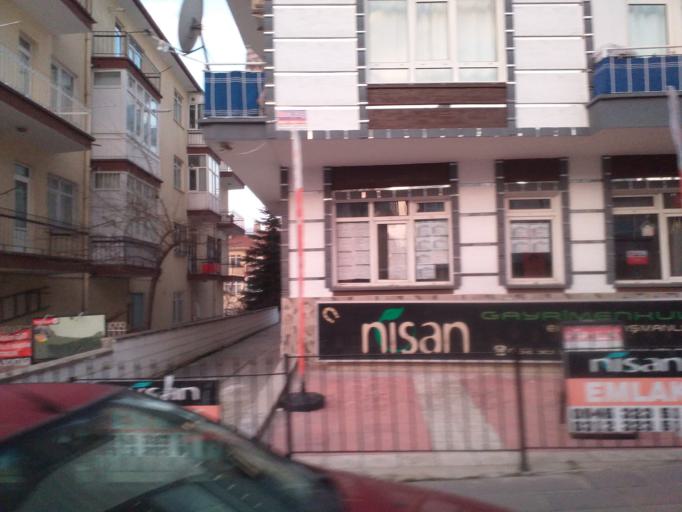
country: TR
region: Ankara
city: Ankara
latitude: 39.9761
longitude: 32.8406
